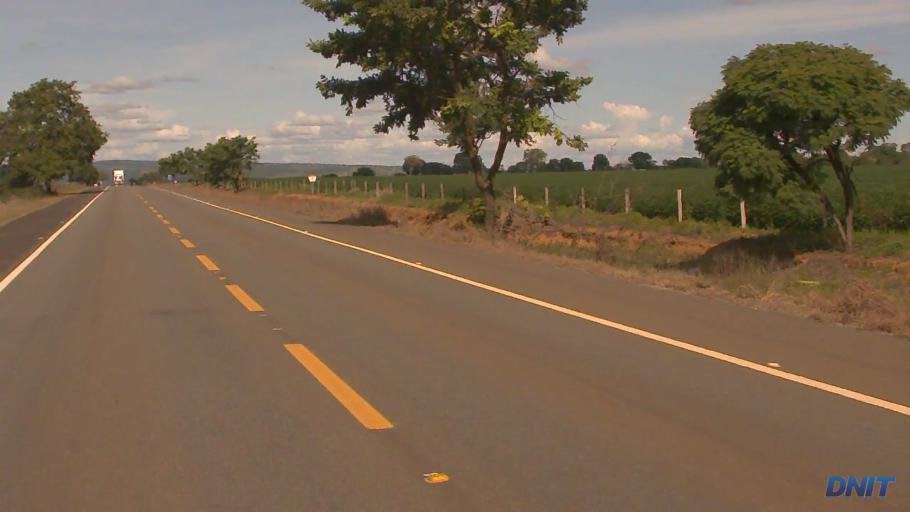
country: BR
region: Goias
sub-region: Padre Bernardo
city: Padre Bernardo
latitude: -15.2181
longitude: -48.6190
